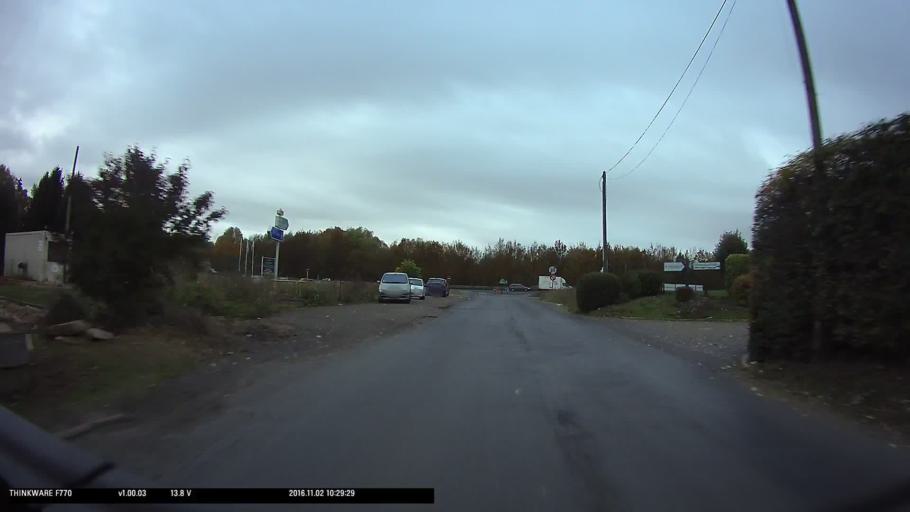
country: FR
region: Ile-de-France
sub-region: Departement du Val-d'Oise
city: Courdimanche
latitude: 49.0599
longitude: 2.0008
